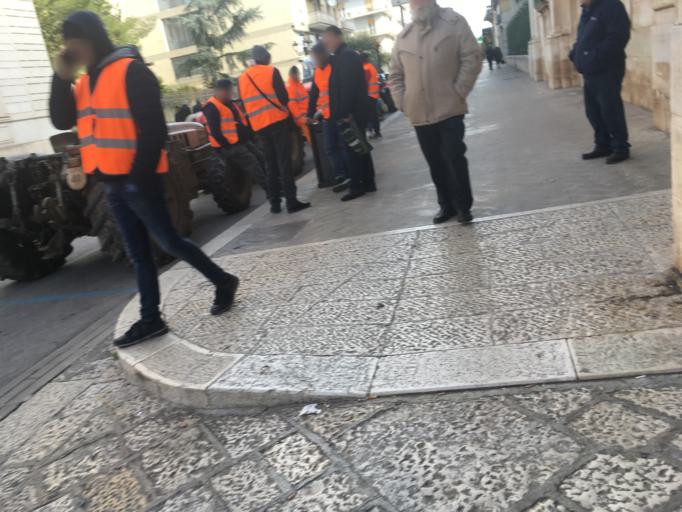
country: IT
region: Apulia
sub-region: Provincia di Bari
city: Bitonto
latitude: 41.1104
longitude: 16.6938
